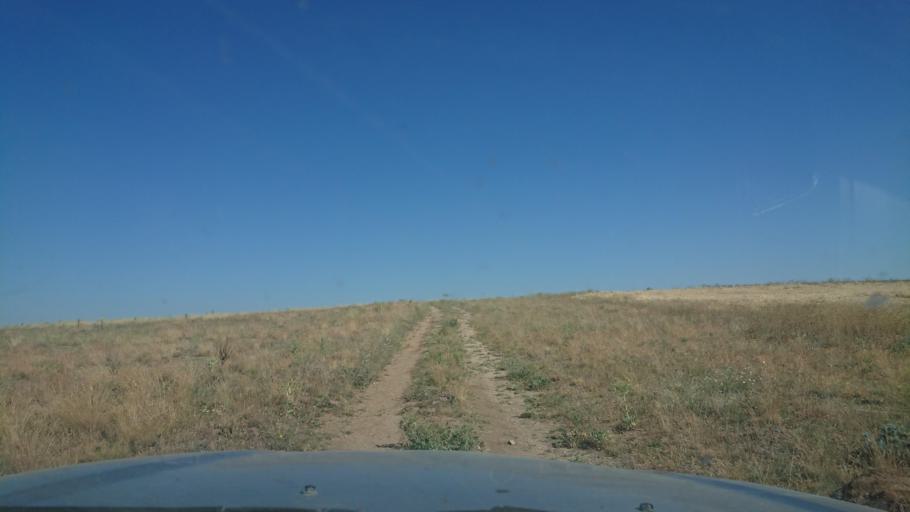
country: TR
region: Aksaray
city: Agacoren
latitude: 38.8385
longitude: 33.9430
